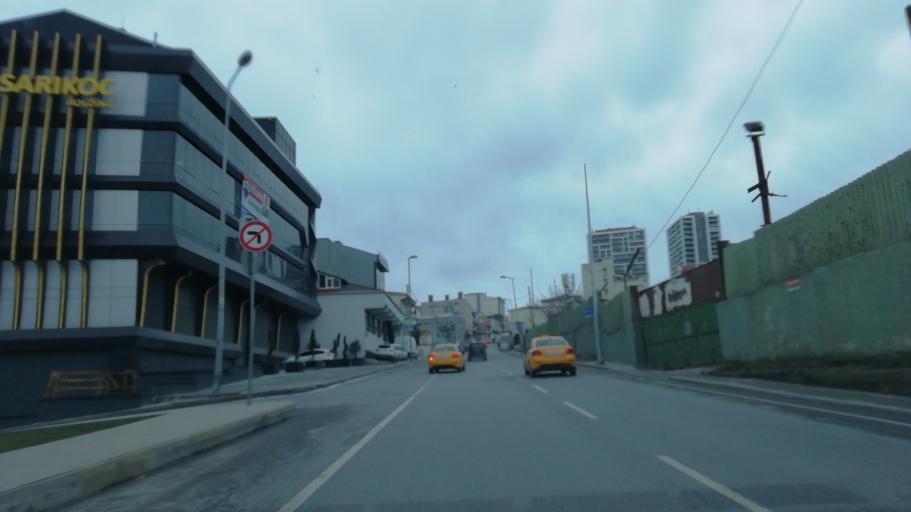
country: TR
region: Istanbul
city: Mahmutbey
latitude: 41.0453
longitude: 28.8249
